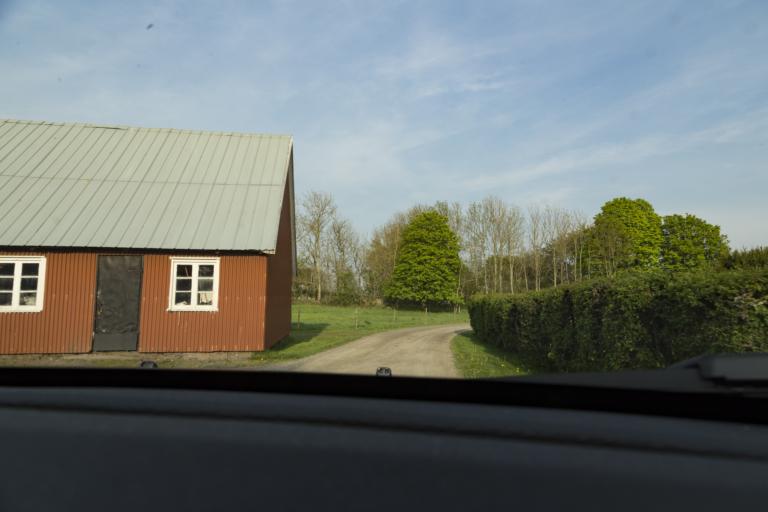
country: SE
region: Halland
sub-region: Varbergs Kommun
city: Varberg
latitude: 57.1601
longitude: 12.2598
